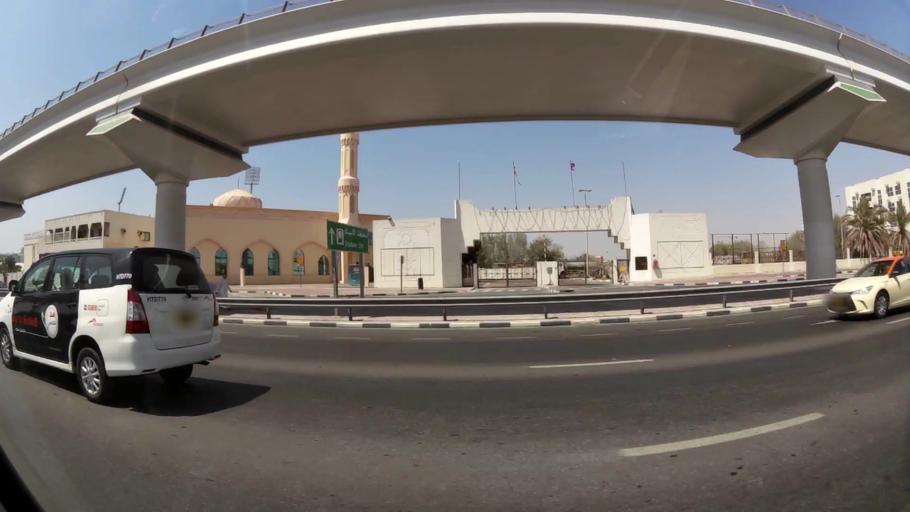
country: AE
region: Ash Shariqah
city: Sharjah
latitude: 25.2757
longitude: 55.3650
